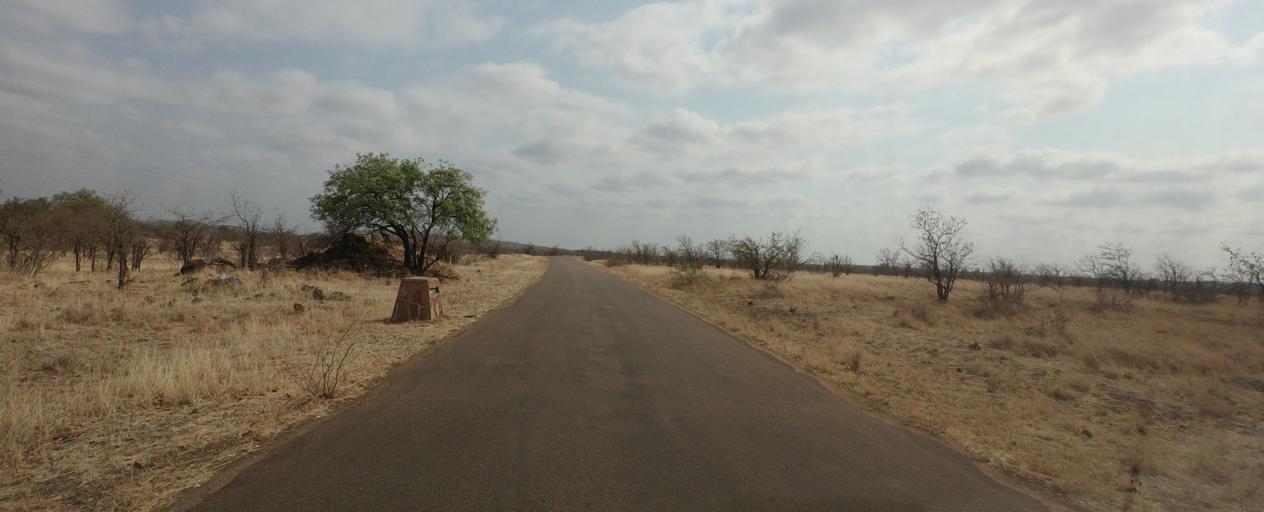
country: ZA
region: Limpopo
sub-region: Vhembe District Municipality
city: Mutale
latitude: -22.5967
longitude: 31.1792
